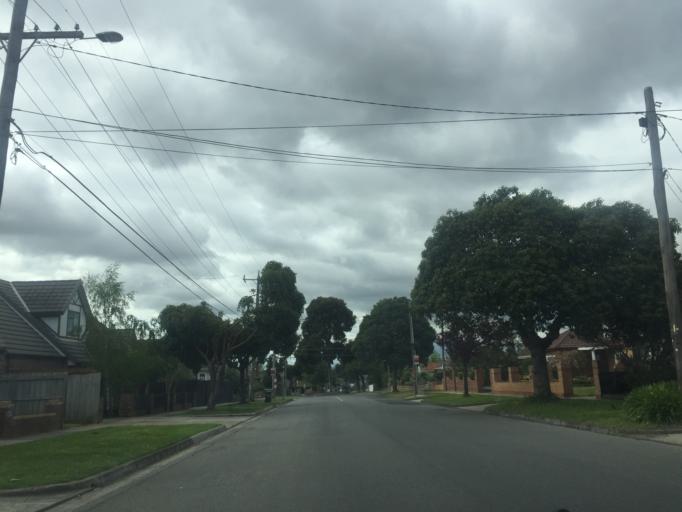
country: AU
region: Victoria
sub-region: Darebin
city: Reservoir
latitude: -37.7215
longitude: 145.0161
